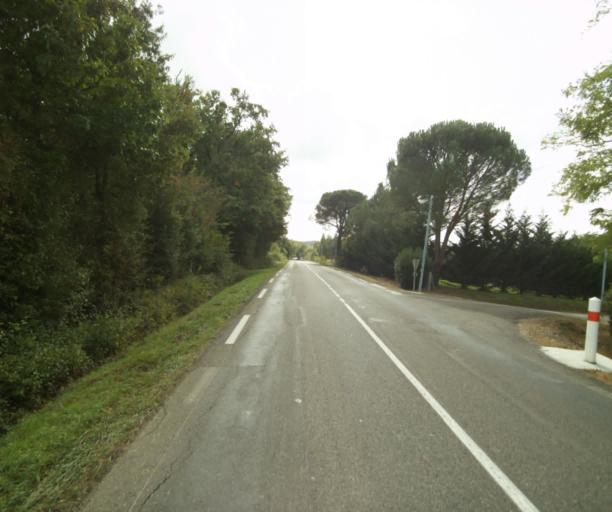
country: FR
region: Midi-Pyrenees
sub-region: Departement du Gers
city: Eauze
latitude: 43.8268
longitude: 0.0911
